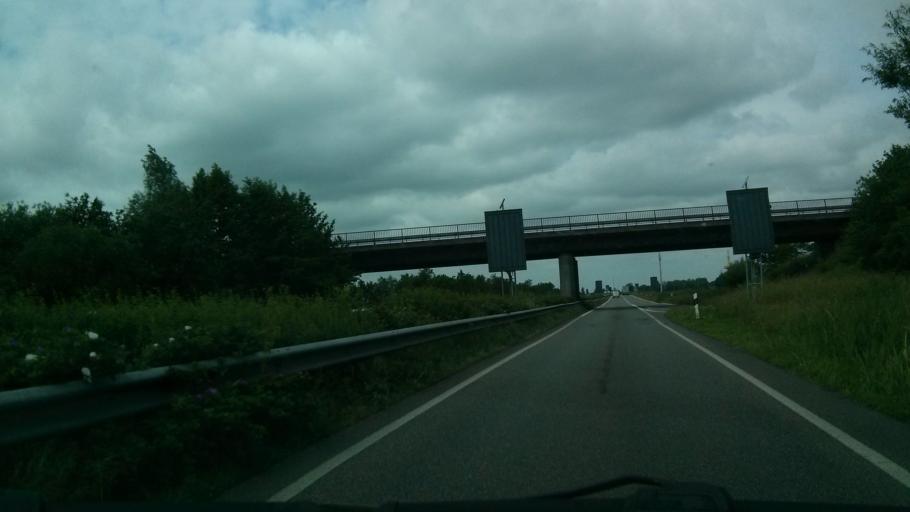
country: DE
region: Lower Saxony
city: Nordenham
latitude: 53.4377
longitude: 8.5182
